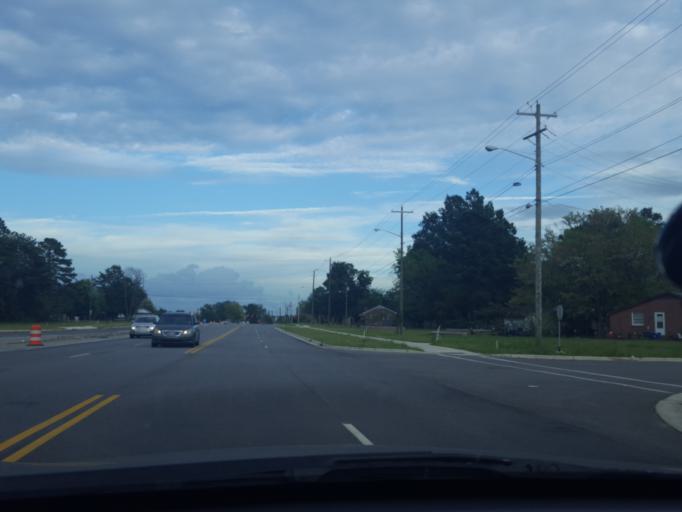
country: US
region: North Carolina
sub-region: Pitt County
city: Greenville
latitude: 35.6080
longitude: -77.3902
